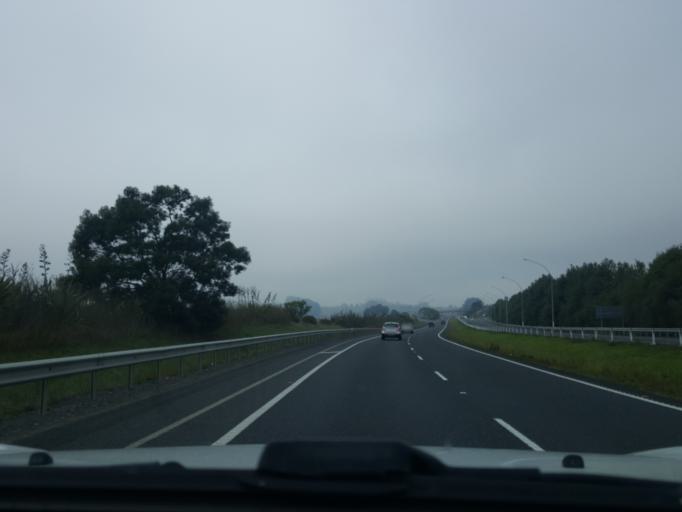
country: NZ
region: Waikato
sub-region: Waikato District
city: Te Kauwhata
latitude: -37.3491
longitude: 175.0778
